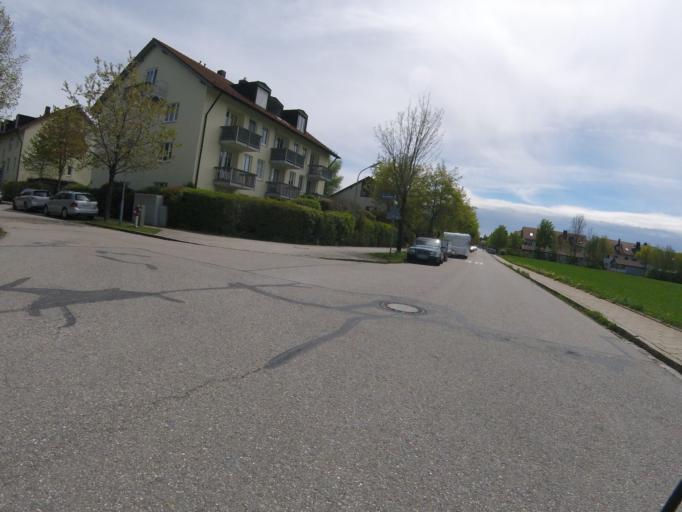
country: DE
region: Bavaria
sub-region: Upper Bavaria
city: Hohenkirchen-Siegertsbrunn
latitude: 48.0226
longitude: 11.7158
